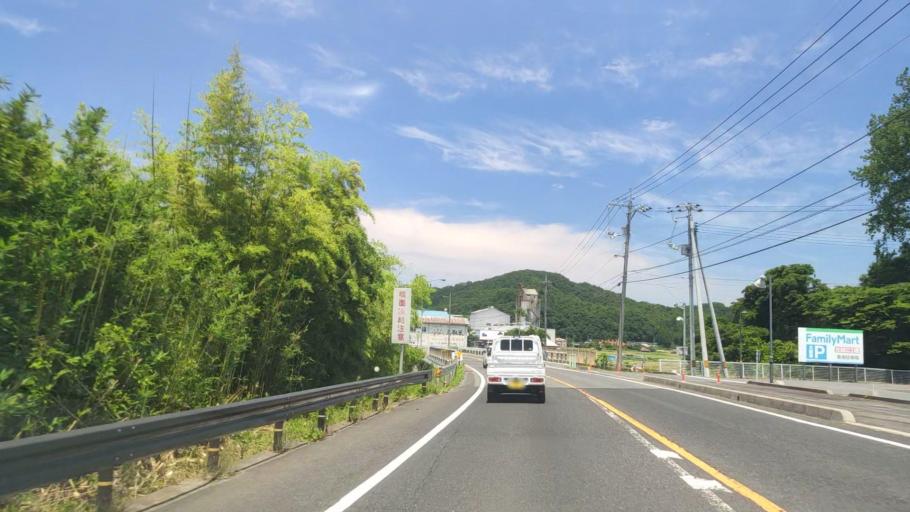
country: JP
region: Tottori
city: Tottori
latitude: 35.4225
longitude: 134.2620
